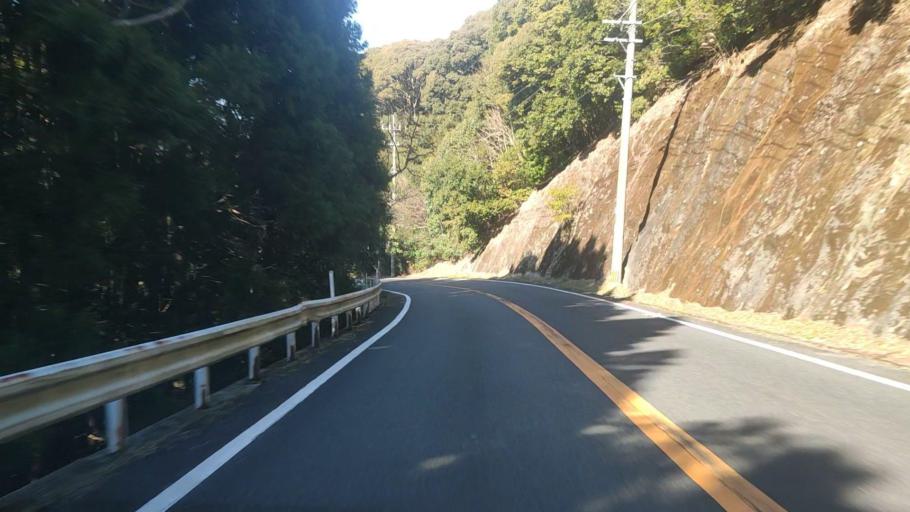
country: JP
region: Oita
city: Saiki
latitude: 32.8969
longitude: 131.9378
